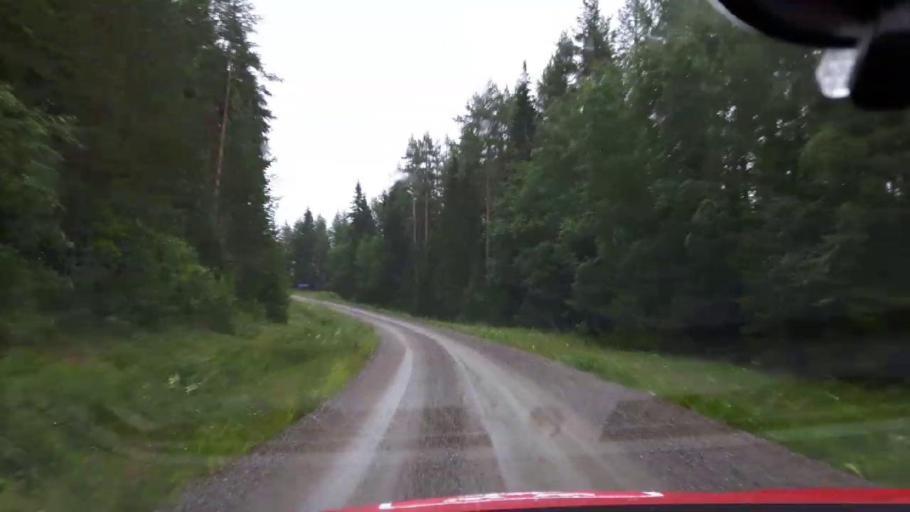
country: SE
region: Jaemtland
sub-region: OEstersunds Kommun
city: Brunflo
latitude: 62.8152
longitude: 14.8944
